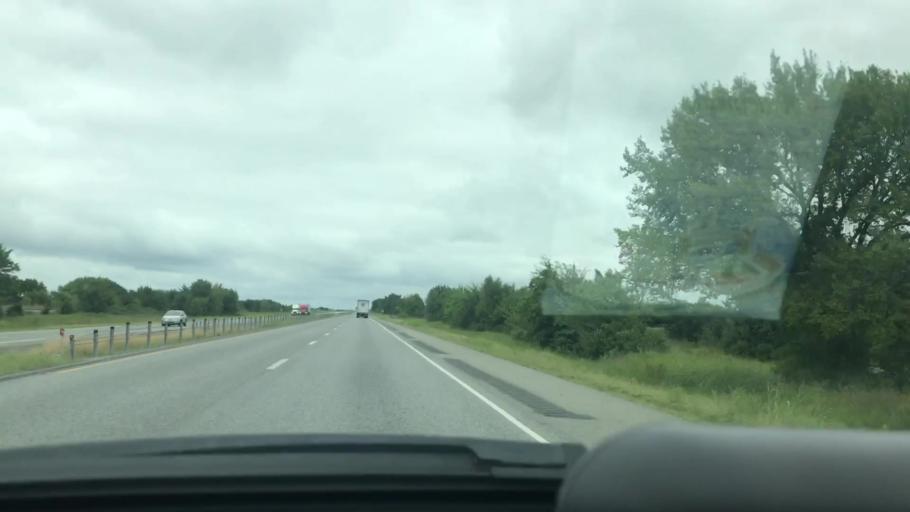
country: US
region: Oklahoma
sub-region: Pittsburg County
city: McAlester
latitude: 34.7437
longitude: -95.8968
